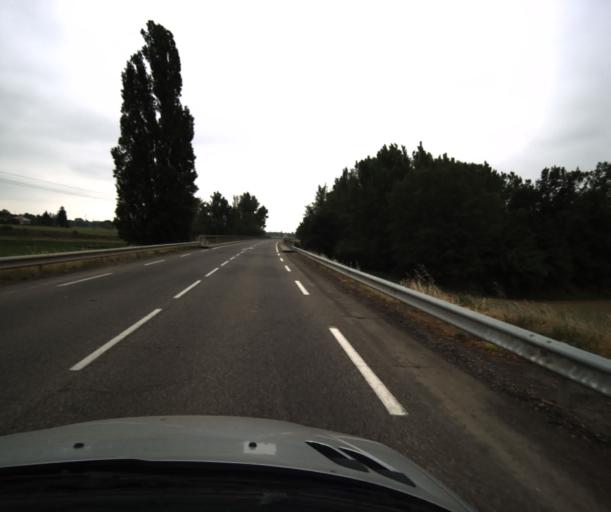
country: FR
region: Midi-Pyrenees
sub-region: Departement du Tarn-et-Garonne
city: Saint-Nicolas-de-la-Grave
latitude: 44.0774
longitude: 0.9945
